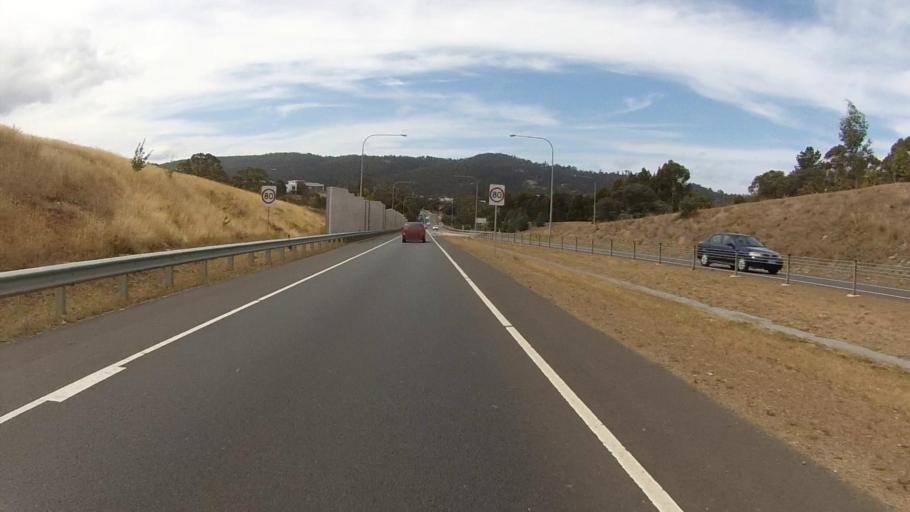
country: AU
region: Tasmania
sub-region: Kingborough
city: Kingston
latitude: -42.9744
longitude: 147.3036
